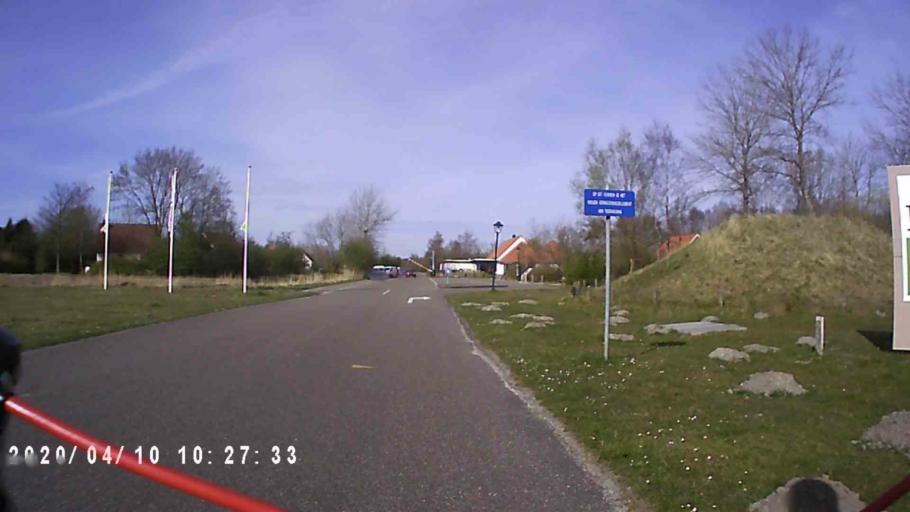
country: NL
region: Friesland
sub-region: Gemeente Dongeradeel
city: Anjum
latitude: 53.3892
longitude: 6.2159
